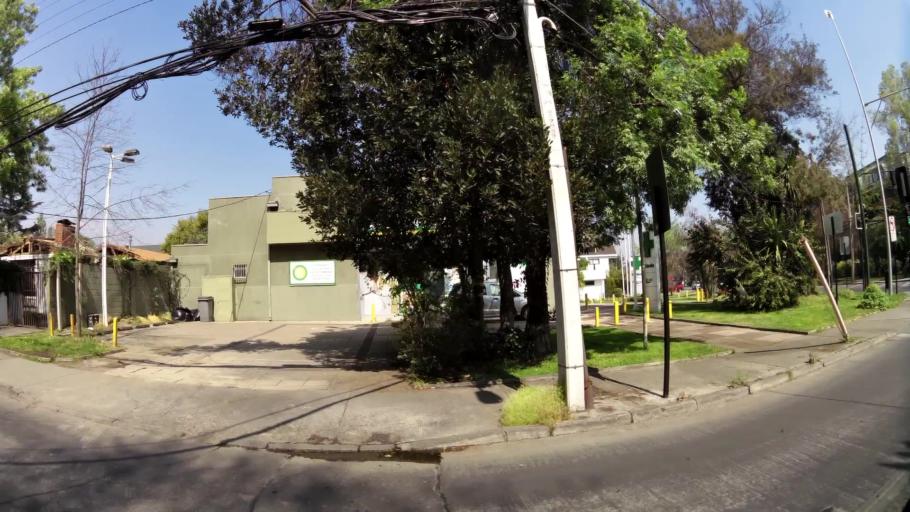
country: CL
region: Santiago Metropolitan
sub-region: Provincia de Santiago
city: Villa Presidente Frei, Nunoa, Santiago, Chile
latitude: -33.3856
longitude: -70.5702
